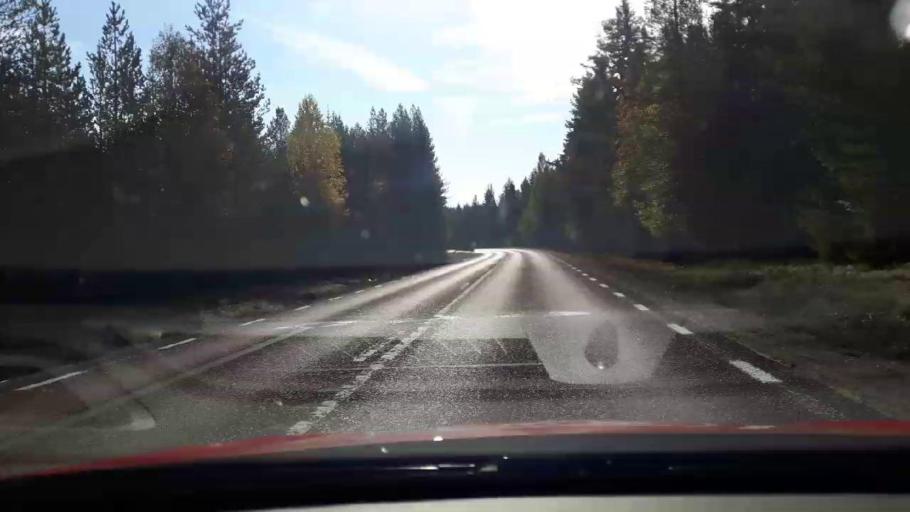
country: SE
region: Gaevleborg
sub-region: Ljusdals Kommun
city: Farila
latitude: 61.9089
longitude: 15.6296
